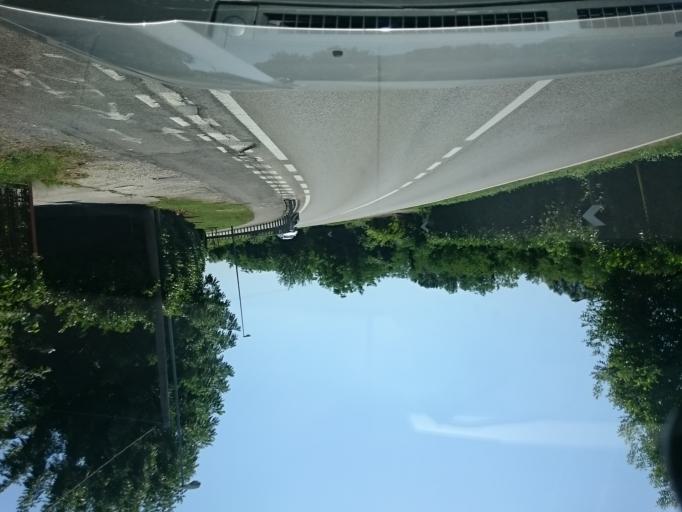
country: IT
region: Veneto
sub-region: Provincia di Padova
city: Villaguattera
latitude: 45.4355
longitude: 11.8271
